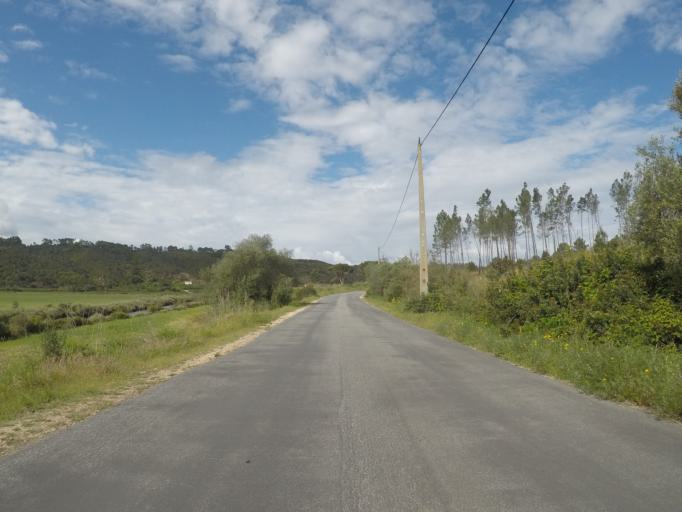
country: PT
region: Beja
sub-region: Odemira
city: Sao Teotonio
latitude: 37.4360
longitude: -8.7780
